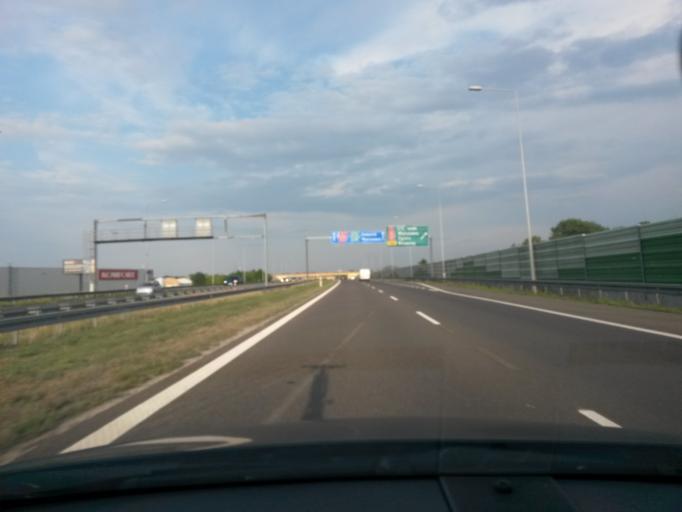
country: PL
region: Lodz Voivodeship
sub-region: Powiat zgierski
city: Strykow
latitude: 51.8890
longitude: 19.5797
